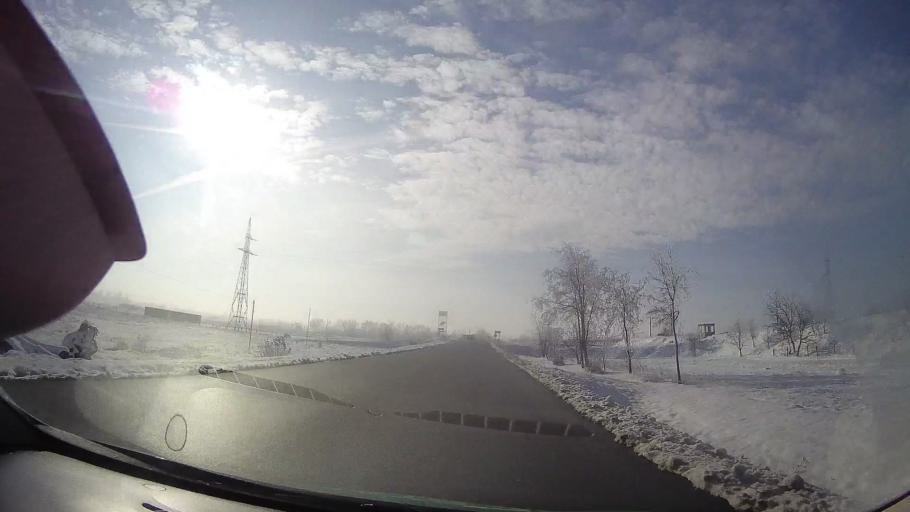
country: RO
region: Neamt
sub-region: Comuna Timisesti
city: Timisesti
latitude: 47.2488
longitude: 26.5472
